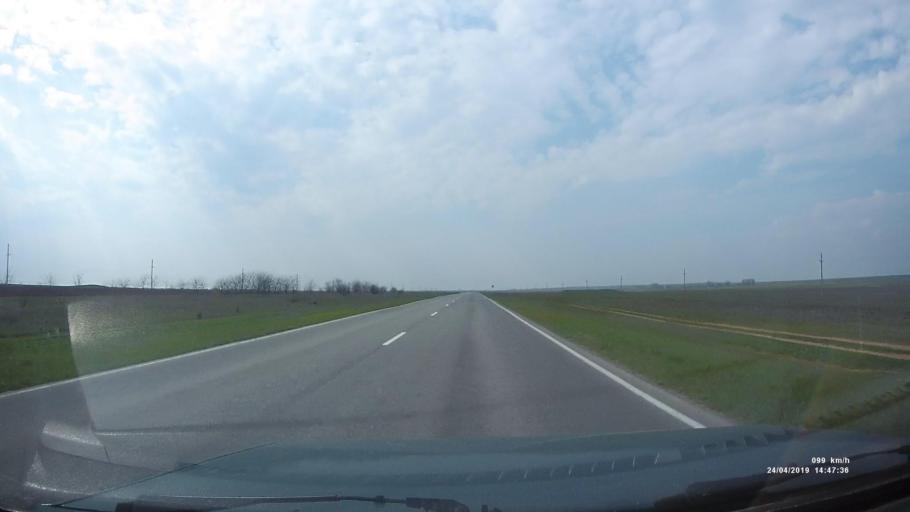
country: RU
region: Rostov
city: Remontnoye
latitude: 46.4930
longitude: 43.7702
